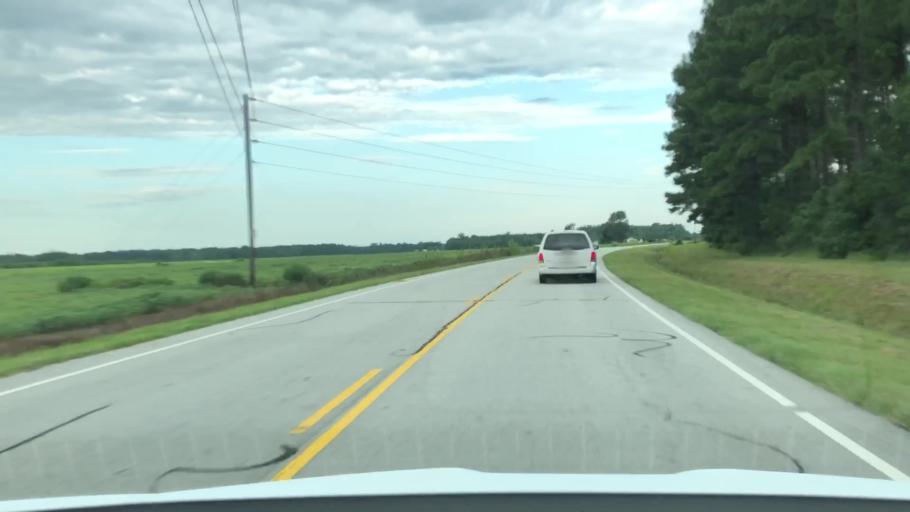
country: US
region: North Carolina
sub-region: Jones County
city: Trenton
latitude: 35.0793
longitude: -77.4293
